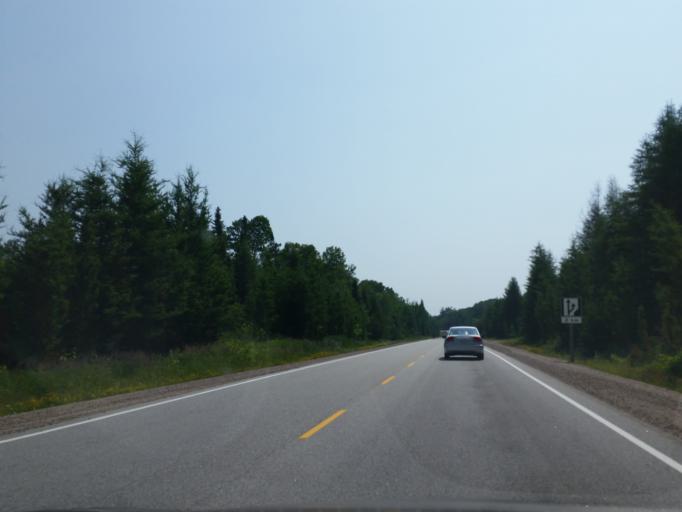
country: CA
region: Ontario
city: Mattawa
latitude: 46.2763
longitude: -78.4734
